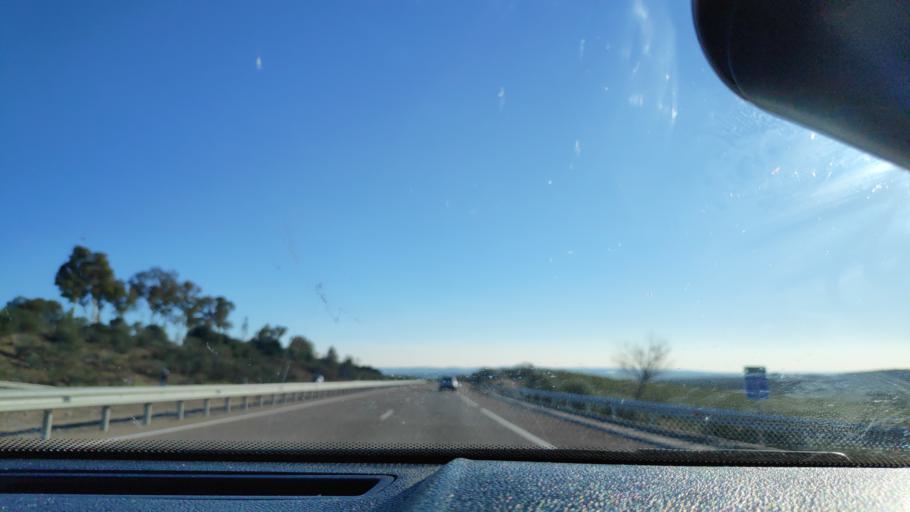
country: ES
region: Andalusia
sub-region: Provincia de Sevilla
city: Guillena
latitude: 37.5614
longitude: -6.1032
